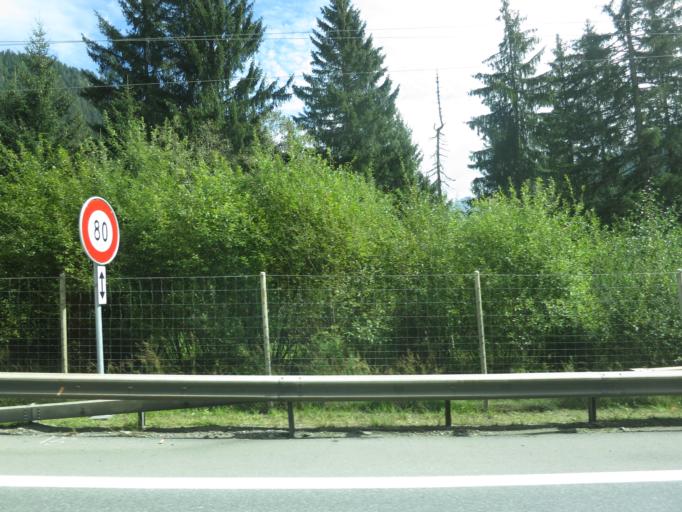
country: CH
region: Grisons
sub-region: Hinterrhein District
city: Thusis
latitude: 46.5684
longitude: 9.3823
